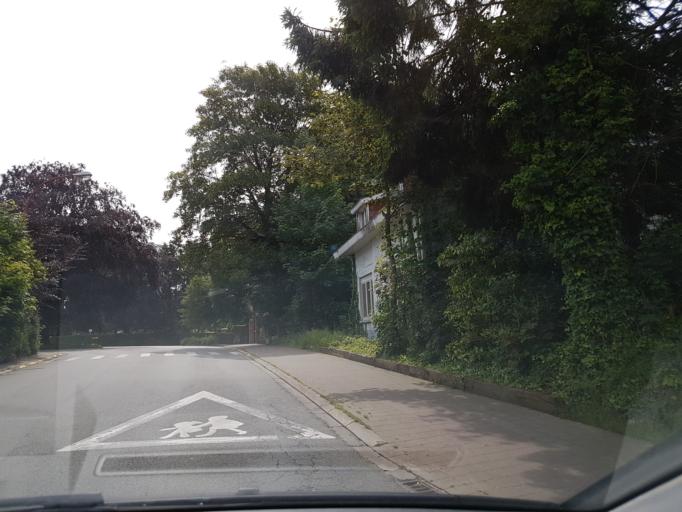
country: BE
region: Flanders
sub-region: Provincie Vlaams-Brabant
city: Asse
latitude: 50.9073
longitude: 4.2024
